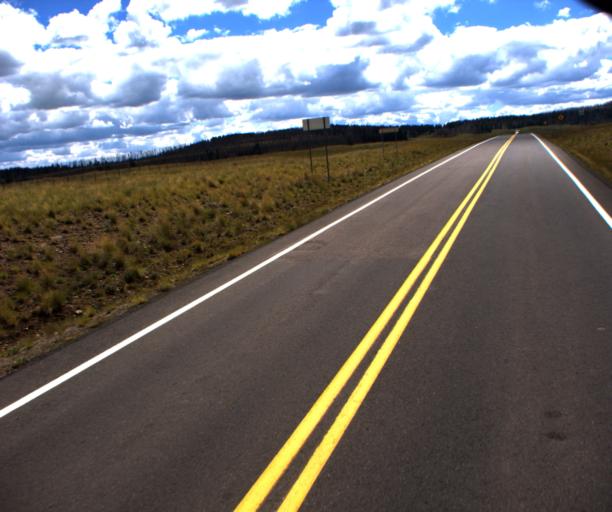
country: US
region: Arizona
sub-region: Apache County
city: Eagar
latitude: 33.9484
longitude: -109.4926
